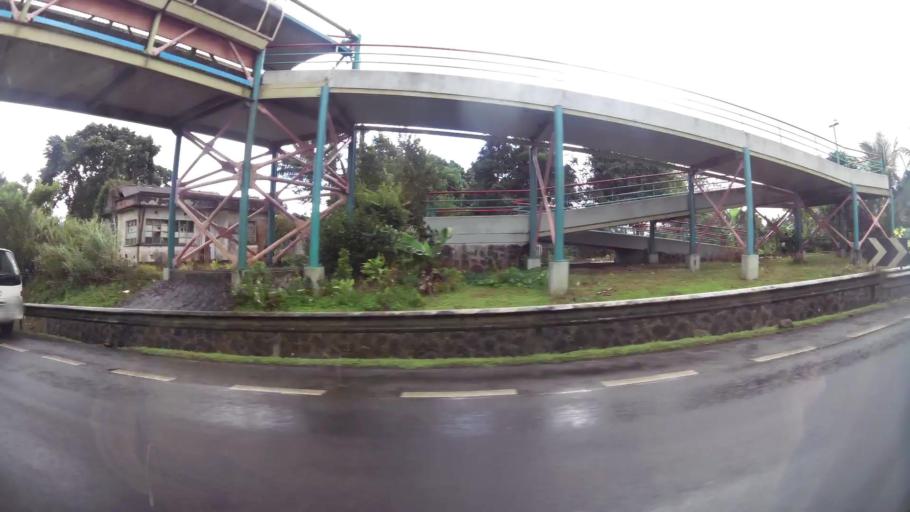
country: MU
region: Plaines Wilhems
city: Curepipe
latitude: -20.2850
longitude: 57.5218
